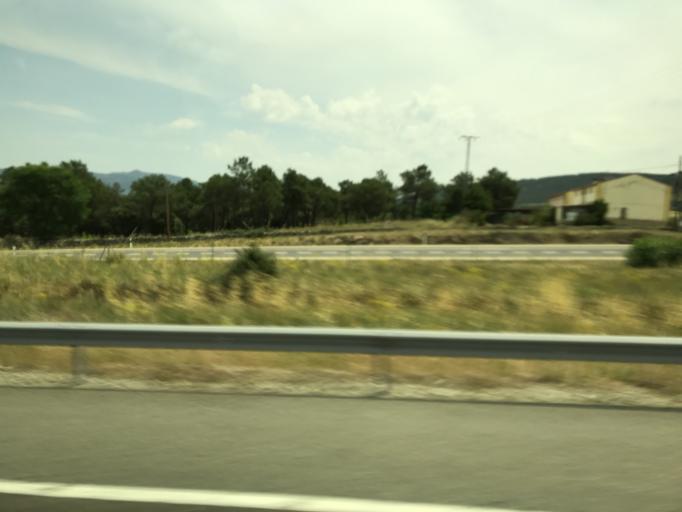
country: ES
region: Madrid
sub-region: Provincia de Madrid
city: Buitrago del Lozoya
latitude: 40.9761
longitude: -3.6388
